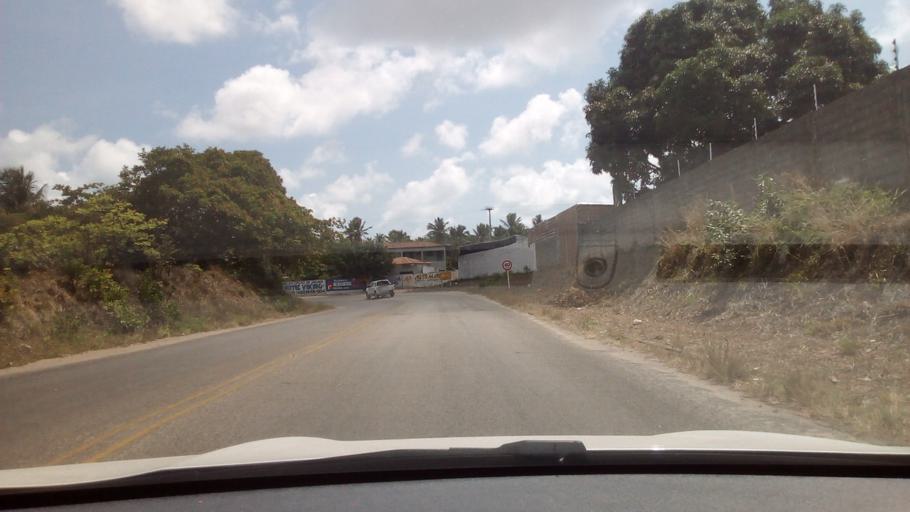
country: BR
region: Paraiba
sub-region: Conde
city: Conde
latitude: -7.2232
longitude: -34.8390
